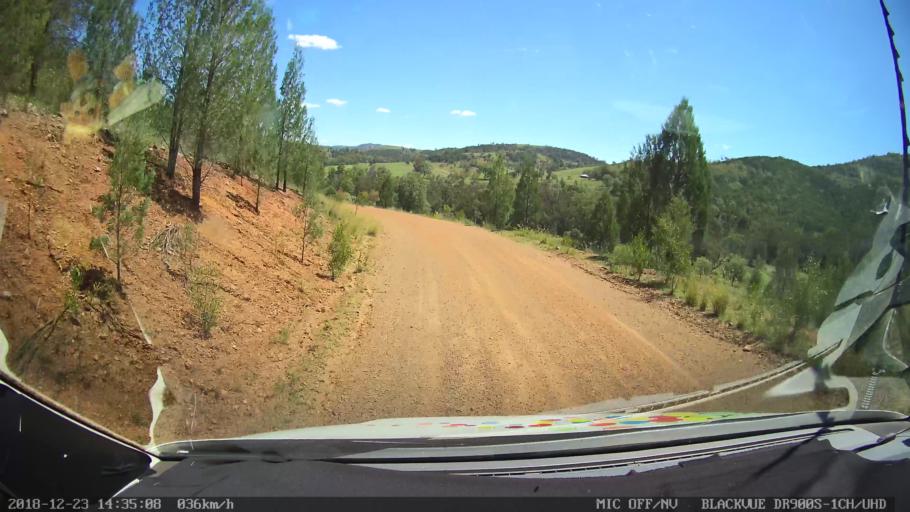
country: AU
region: New South Wales
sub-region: Tamworth Municipality
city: Manilla
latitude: -30.6085
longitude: 150.9079
